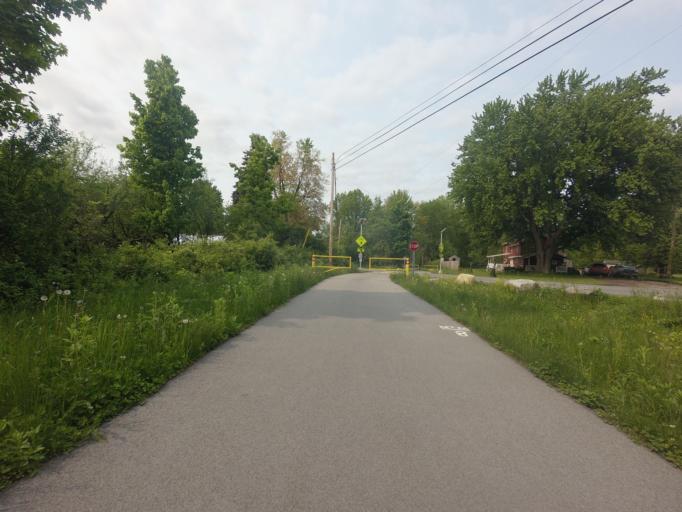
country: US
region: New York
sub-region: Jefferson County
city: Watertown
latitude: 43.9738
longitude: -75.8625
